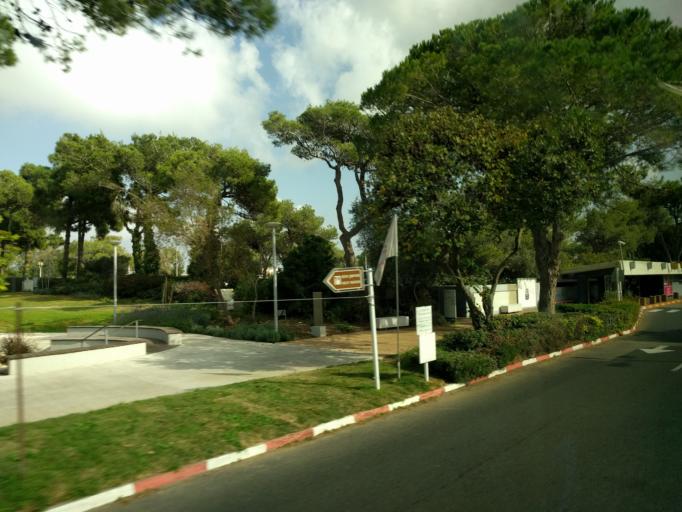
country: IL
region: Haifa
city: Nesher
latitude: 32.7591
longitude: 35.0215
